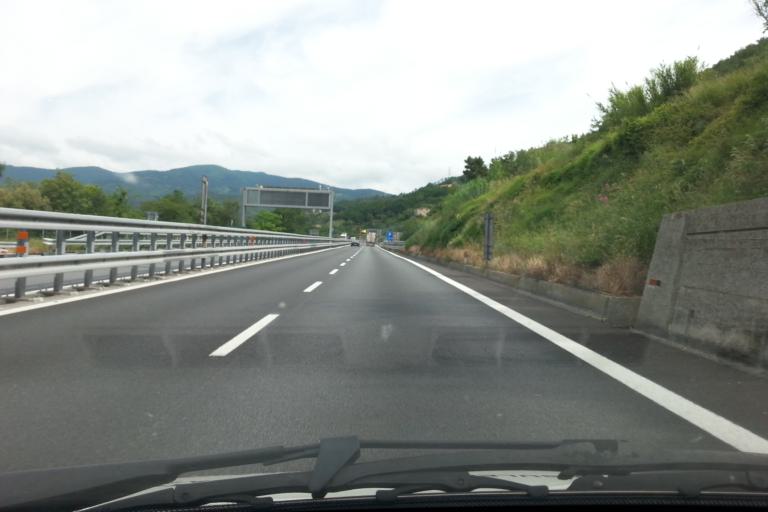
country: IT
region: Liguria
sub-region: Provincia di Savona
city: Calice Ligure
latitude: 44.1923
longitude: 8.3062
